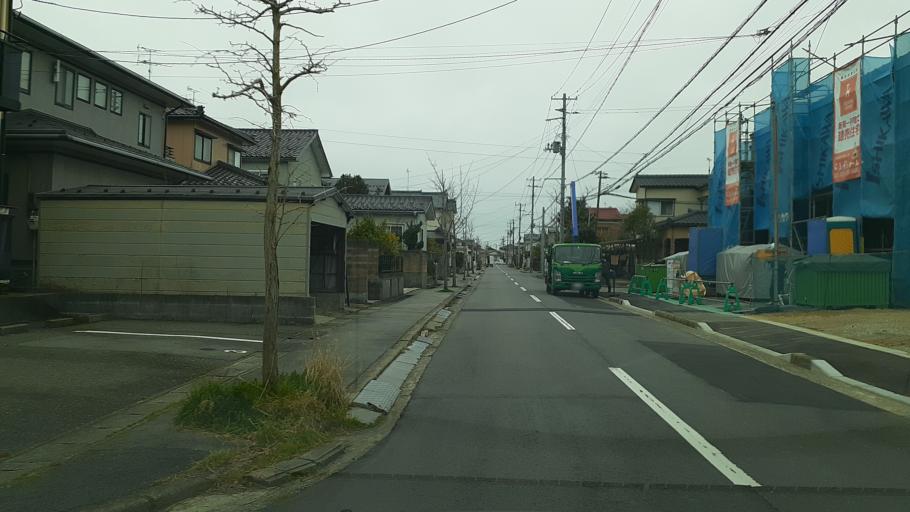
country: JP
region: Niigata
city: Niigata-shi
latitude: 37.8617
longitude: 139.0393
